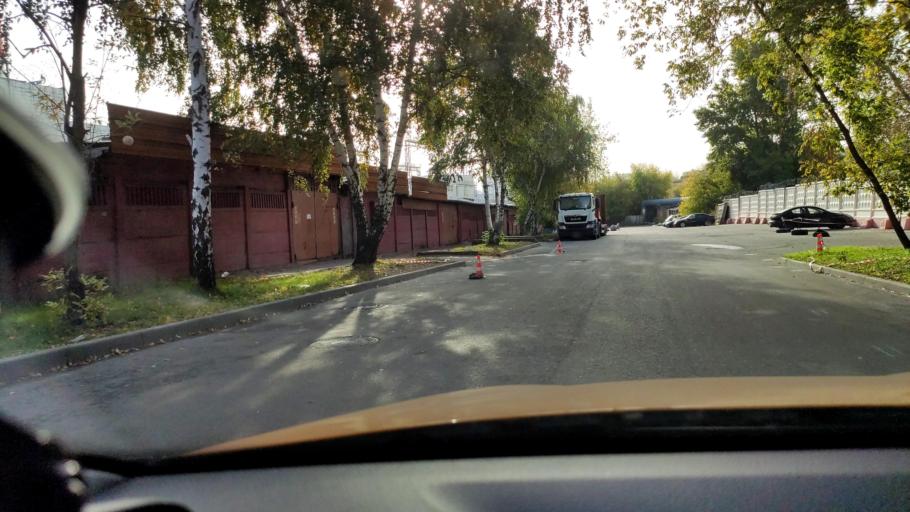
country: RU
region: Moscow
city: Novyye Cheremushki
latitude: 55.6992
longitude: 37.5829
